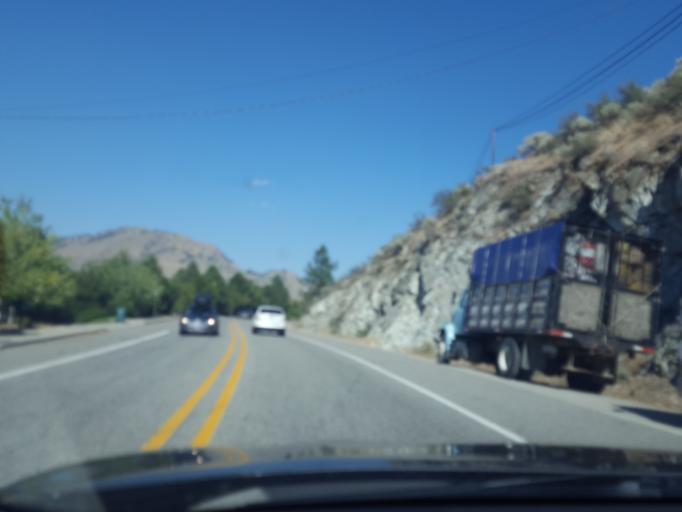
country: US
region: Washington
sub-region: Chelan County
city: Chelan
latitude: 47.8359
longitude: -120.0336
